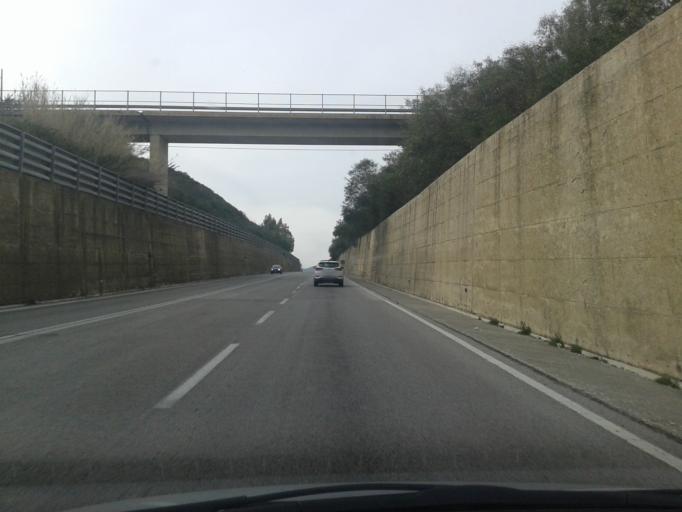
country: IT
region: Sicily
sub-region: Palermo
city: Giacalone
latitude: 38.0319
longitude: 13.2570
